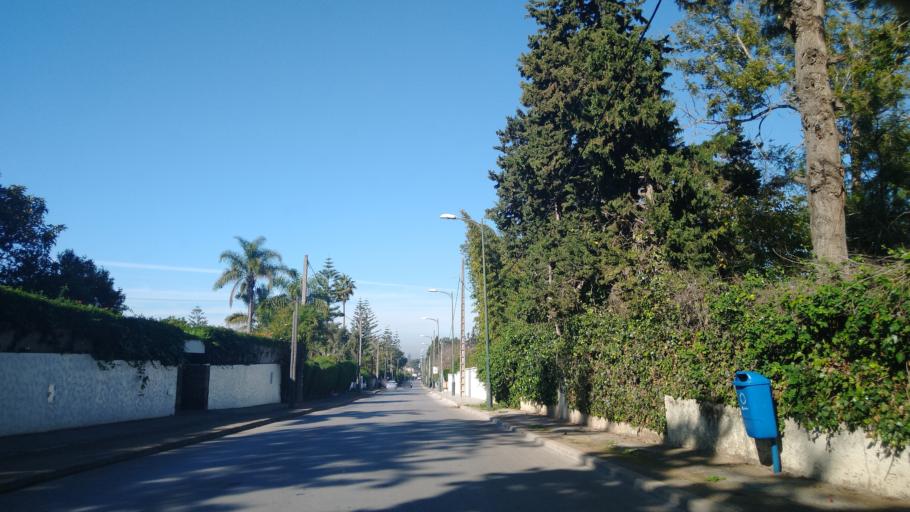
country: MA
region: Rabat-Sale-Zemmour-Zaer
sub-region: Rabat
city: Rabat
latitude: 33.9663
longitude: -6.8513
